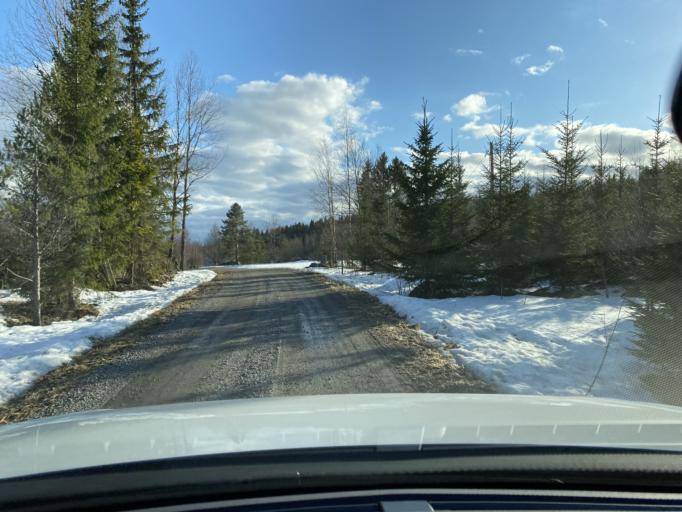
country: FI
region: Pirkanmaa
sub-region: Lounais-Pirkanmaa
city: Mouhijaervi
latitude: 61.4582
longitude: 22.9588
